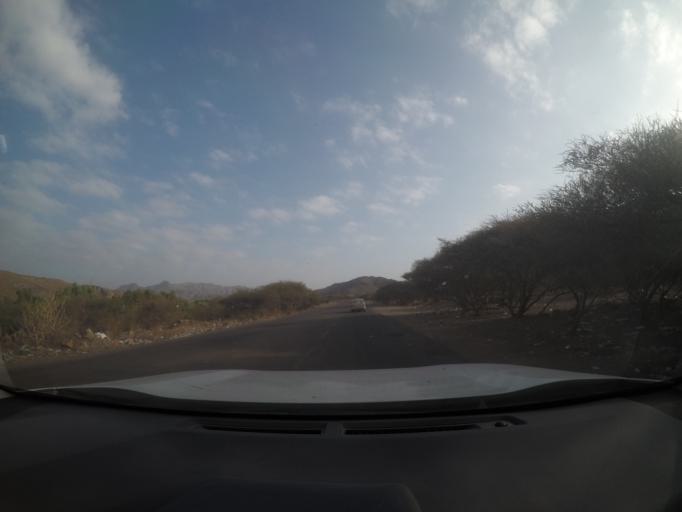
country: YE
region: Lahij
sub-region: Al Milah
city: Al Milah
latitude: 13.3349
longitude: 44.7601
